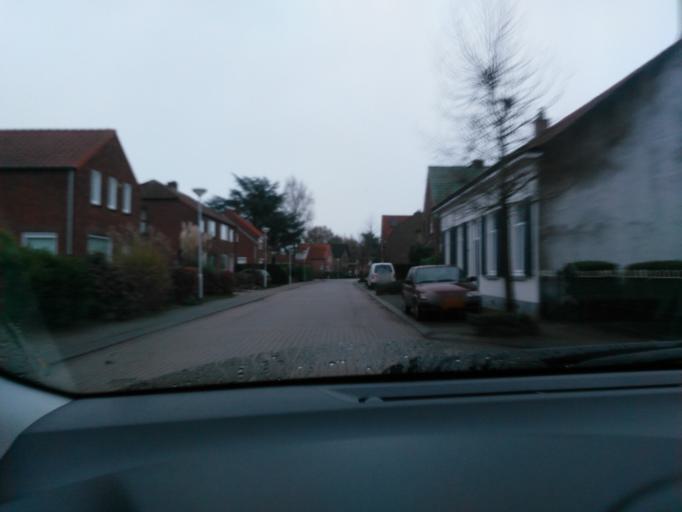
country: NL
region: Zeeland
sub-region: Gemeente Hulst
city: Hulst
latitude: 51.2598
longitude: 4.0564
